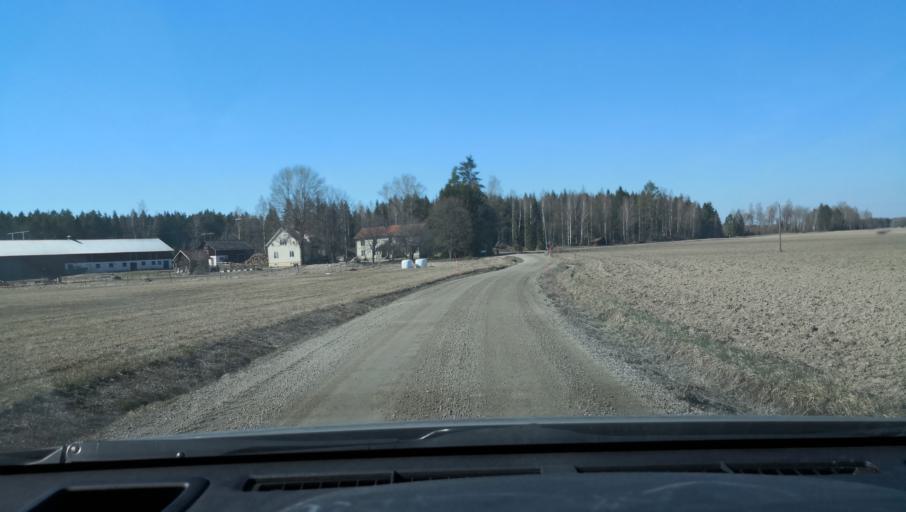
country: SE
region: Vaestmanland
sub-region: Sala Kommun
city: Sala
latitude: 59.8833
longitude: 16.5294
